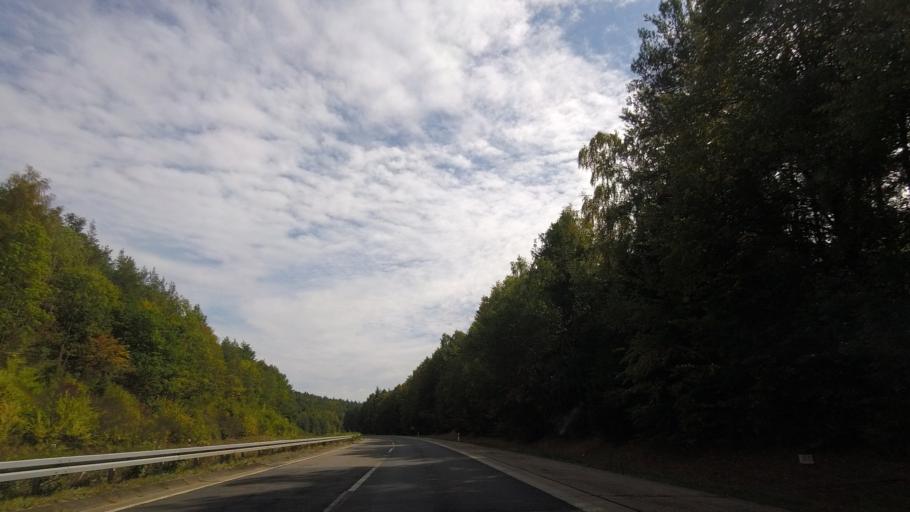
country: DE
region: Hesse
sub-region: Regierungsbezirk Kassel
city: Kirchheim
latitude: 50.8067
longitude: 9.5196
